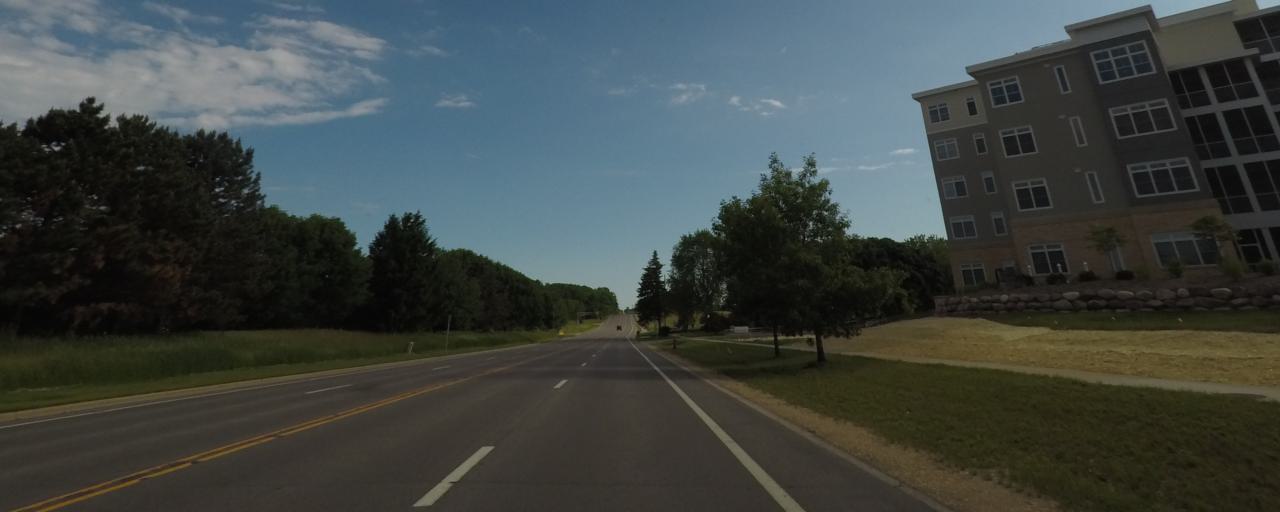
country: US
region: Wisconsin
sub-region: Dane County
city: Sun Prairie
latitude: 43.1560
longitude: -89.2854
